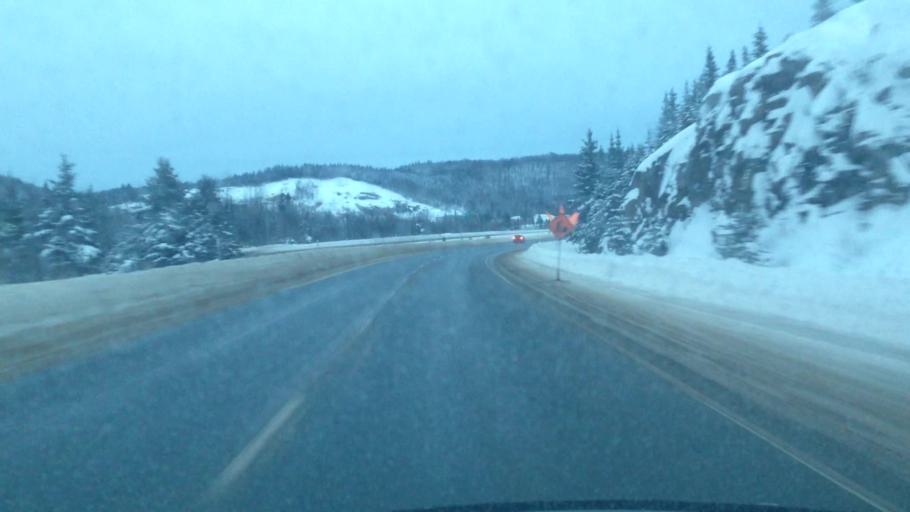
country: CA
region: Quebec
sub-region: Laurentides
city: Mont-Tremblant
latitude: 46.1184
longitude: -74.4638
